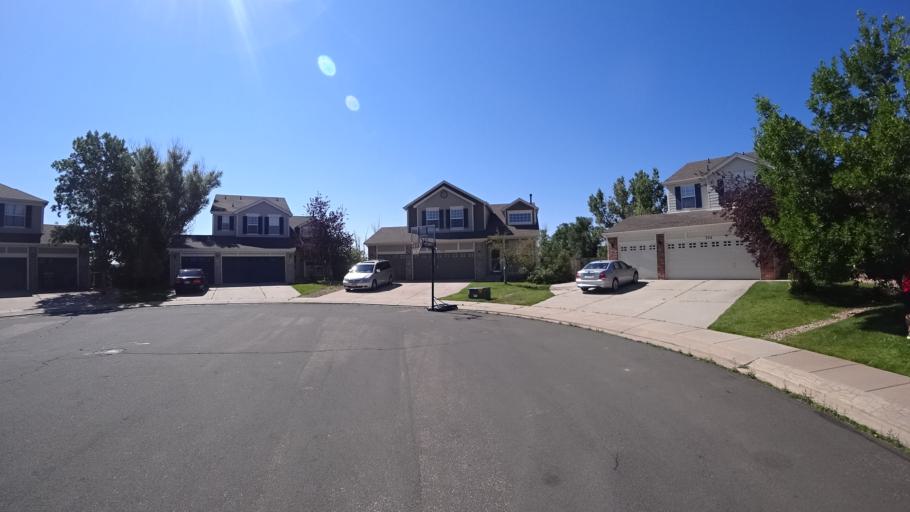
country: US
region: Colorado
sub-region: El Paso County
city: Black Forest
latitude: 38.9434
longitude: -104.7436
